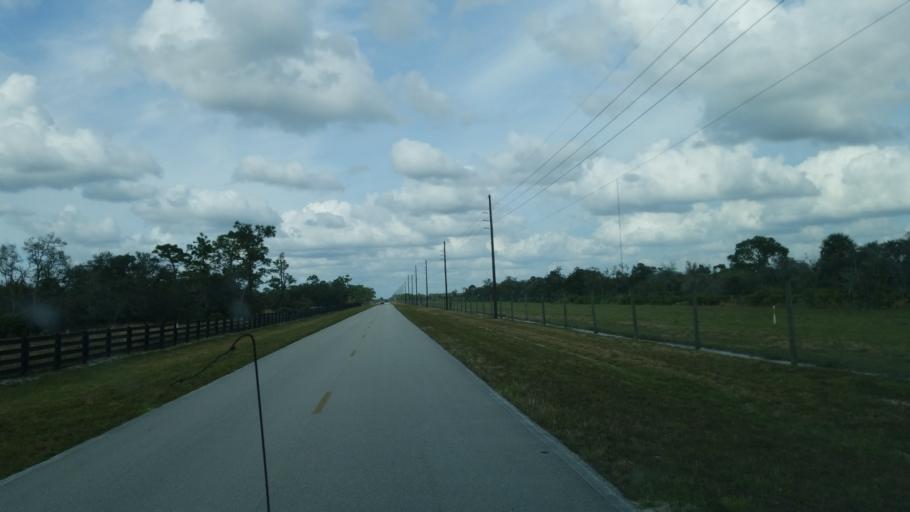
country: US
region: Florida
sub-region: Okeechobee County
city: Cypress Quarters
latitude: 27.4918
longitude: -80.7738
